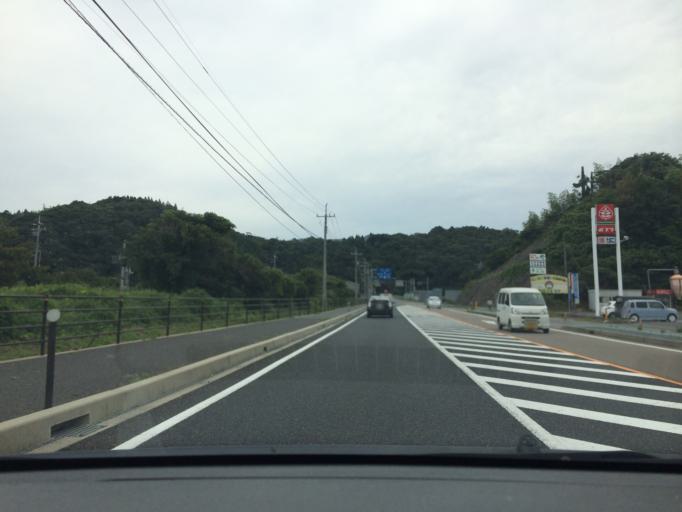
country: JP
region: Shimane
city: Masuda
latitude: 34.7227
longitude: 131.8660
